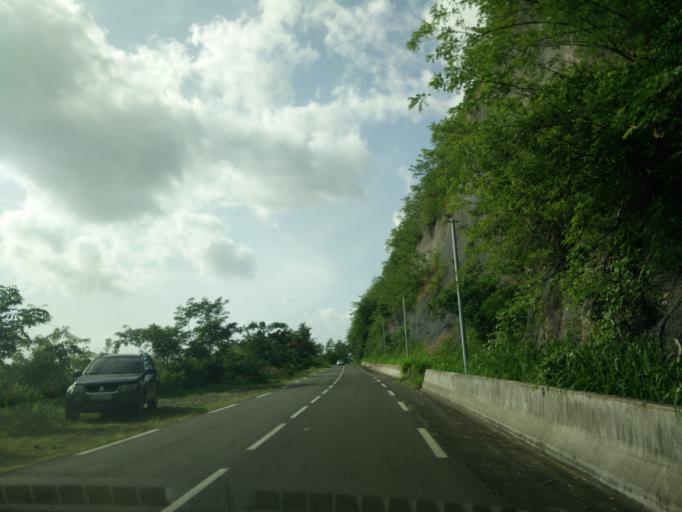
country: MQ
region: Martinique
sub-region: Martinique
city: Saint-Pierre
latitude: 14.8097
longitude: -61.2278
